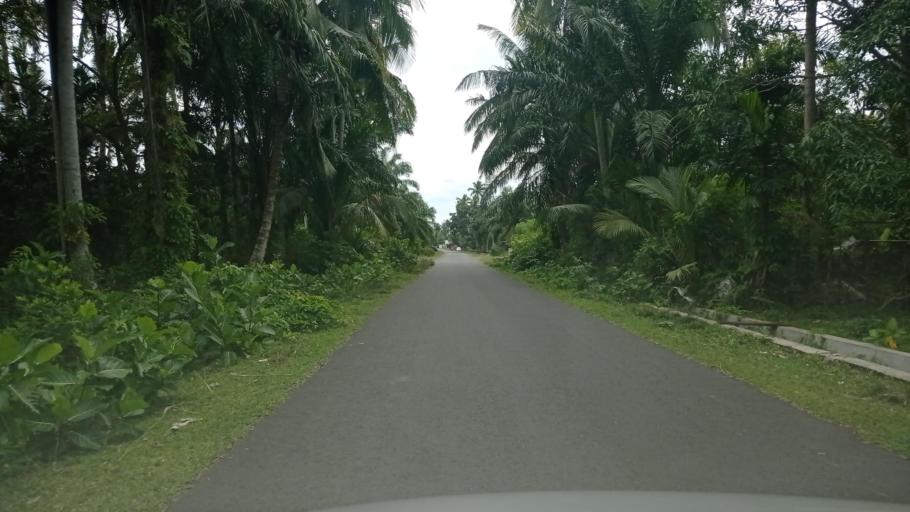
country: ID
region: Bengkulu
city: Ipuh
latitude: -2.5785
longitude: 101.1164
